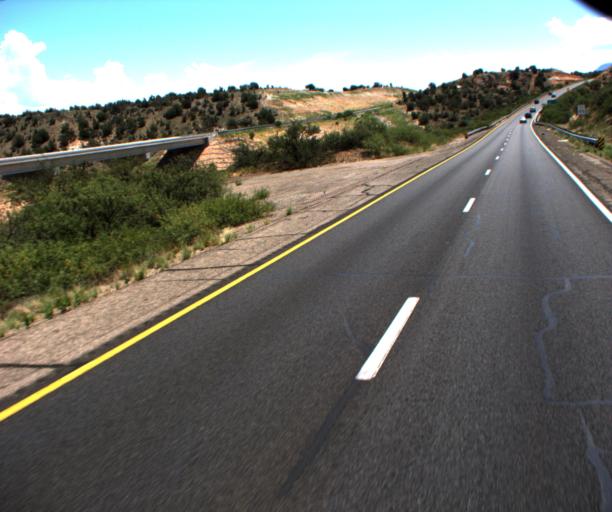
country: US
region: Arizona
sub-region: Yavapai County
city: Verde Village
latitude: 34.6792
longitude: -111.9740
